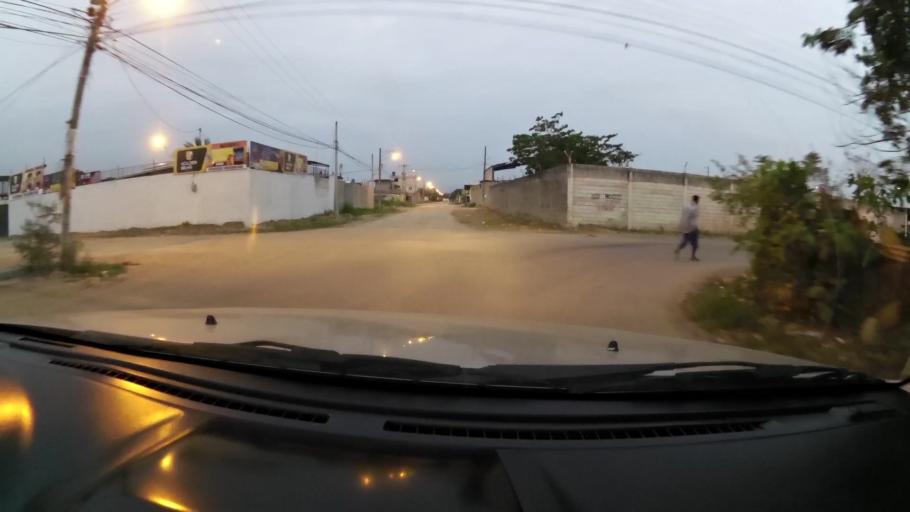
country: EC
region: El Oro
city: Machala
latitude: -3.2621
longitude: -79.9340
